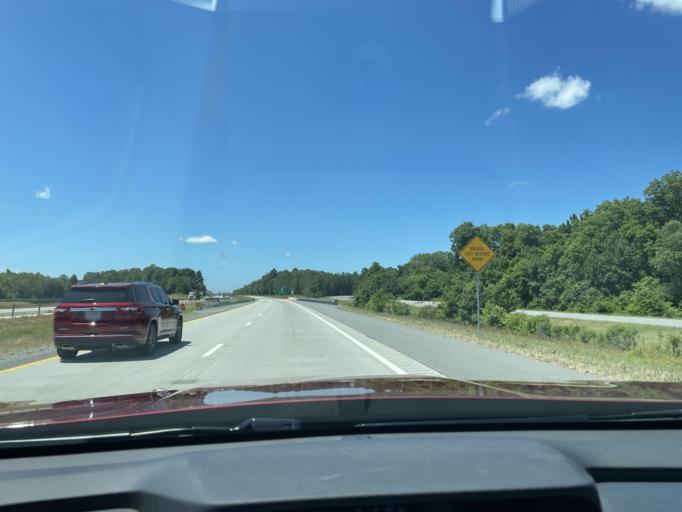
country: US
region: Arkansas
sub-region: Jefferson County
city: Pine Bluff
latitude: 34.1950
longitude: -91.9765
